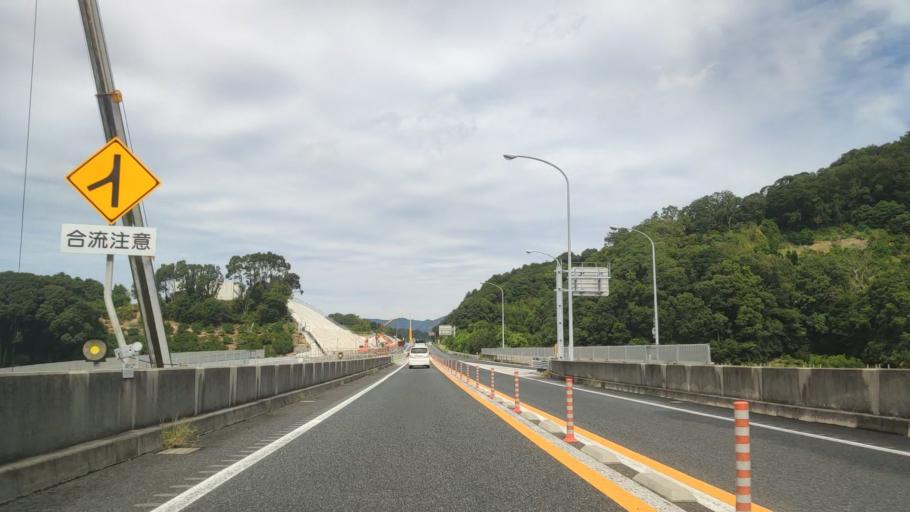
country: JP
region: Wakayama
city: Kainan
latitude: 34.0291
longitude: 135.2009
